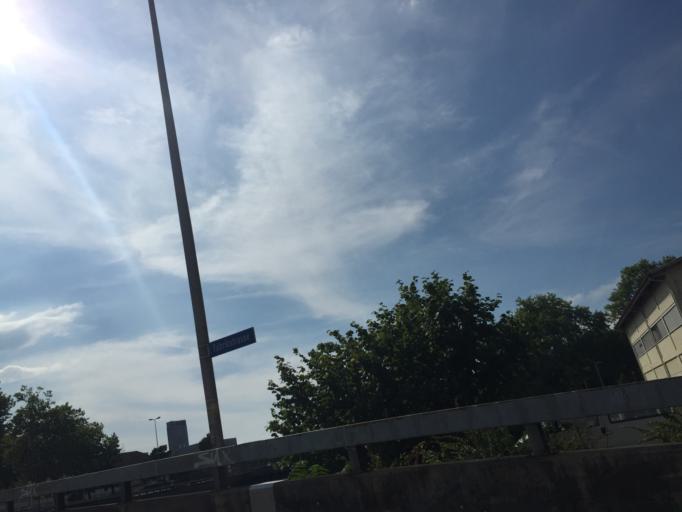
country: CH
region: Bern
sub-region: Bern-Mittelland District
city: Bern
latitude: 46.9520
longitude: 7.4226
